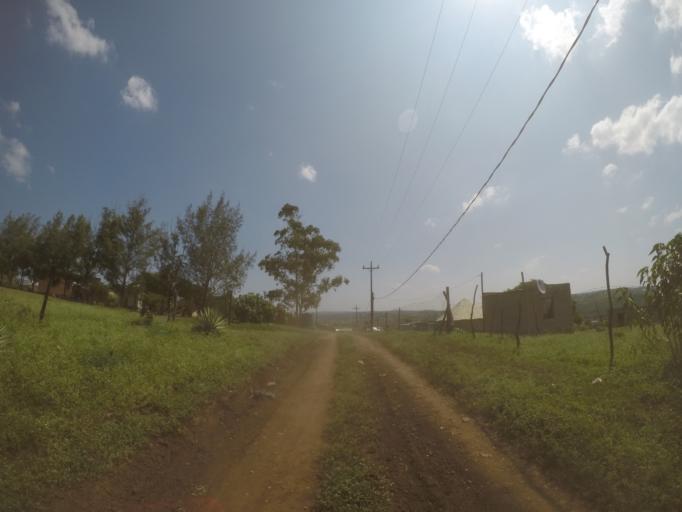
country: ZA
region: KwaZulu-Natal
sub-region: uThungulu District Municipality
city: Empangeni
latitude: -28.5901
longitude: 31.7428
